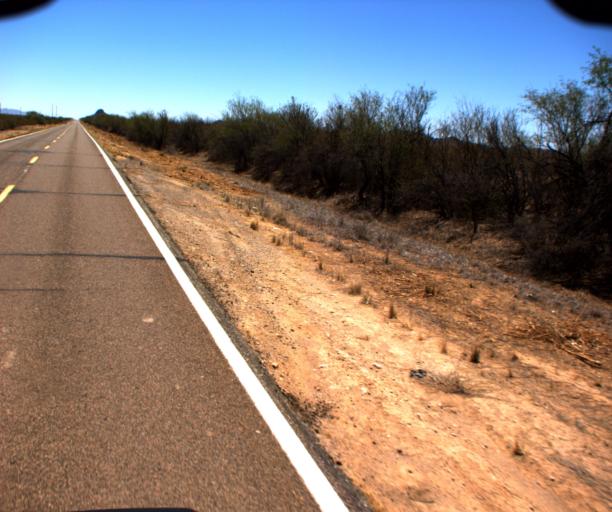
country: US
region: Arizona
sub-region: Pima County
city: Ajo
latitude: 32.2073
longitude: -112.5876
